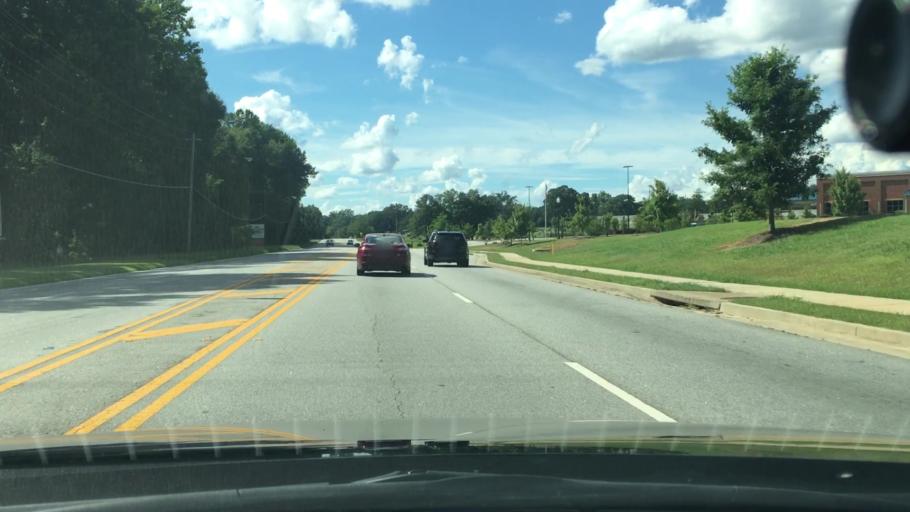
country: US
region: Georgia
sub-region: Spalding County
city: Griffin
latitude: 33.2416
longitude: -84.2487
